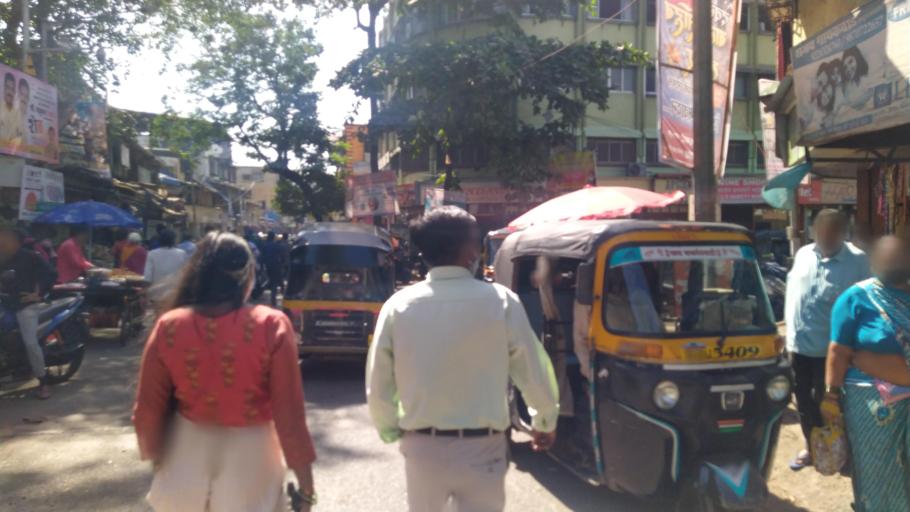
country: IN
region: Maharashtra
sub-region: Mumbai Suburban
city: Mumbai
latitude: 19.0654
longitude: 72.8770
